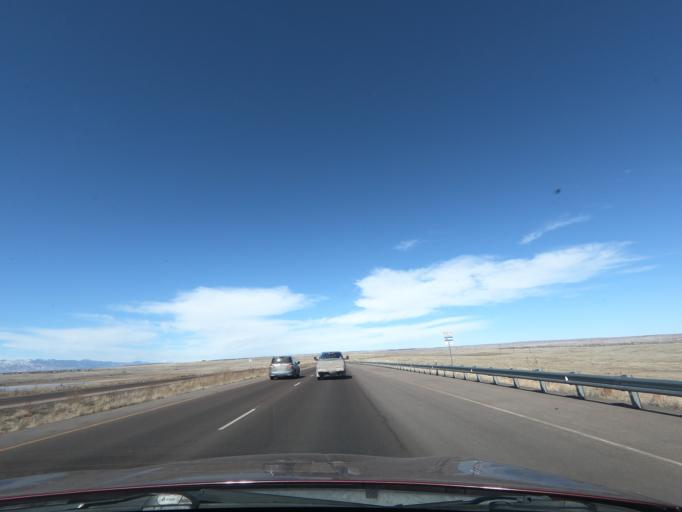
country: US
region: Colorado
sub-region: El Paso County
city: Security-Widefield
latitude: 38.7394
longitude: -104.6825
